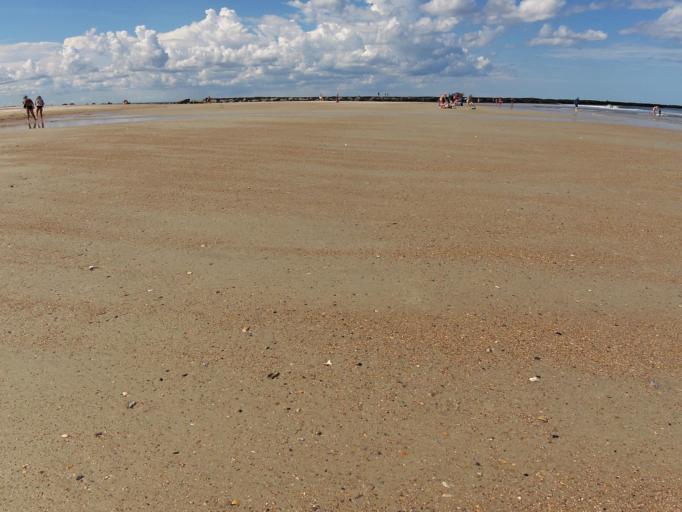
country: US
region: Florida
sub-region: Nassau County
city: Fernandina Beach
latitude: 30.7000
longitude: -81.4260
